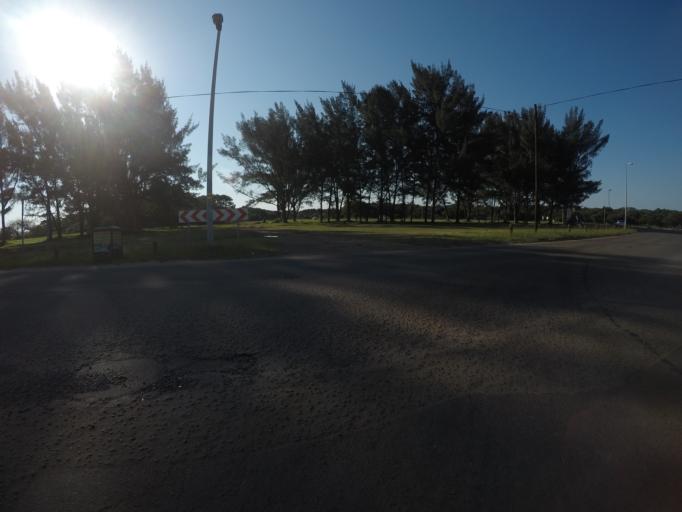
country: ZA
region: KwaZulu-Natal
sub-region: uThungulu District Municipality
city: Richards Bay
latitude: -28.7870
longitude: 32.0834
